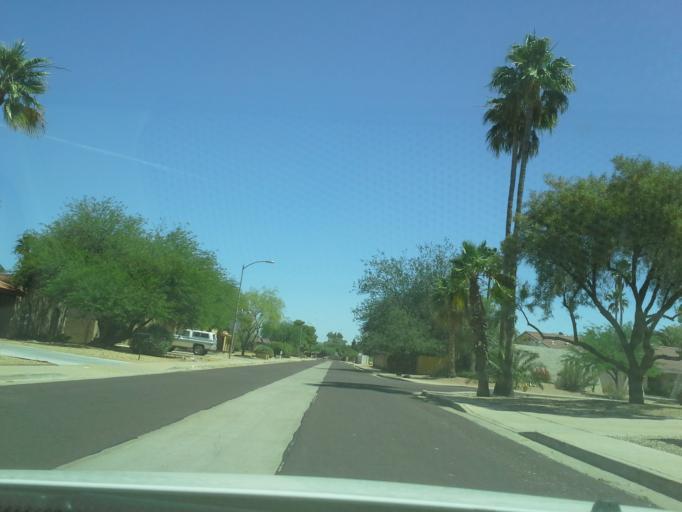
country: US
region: Arizona
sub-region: Maricopa County
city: Paradise Valley
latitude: 33.6084
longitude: -111.9558
